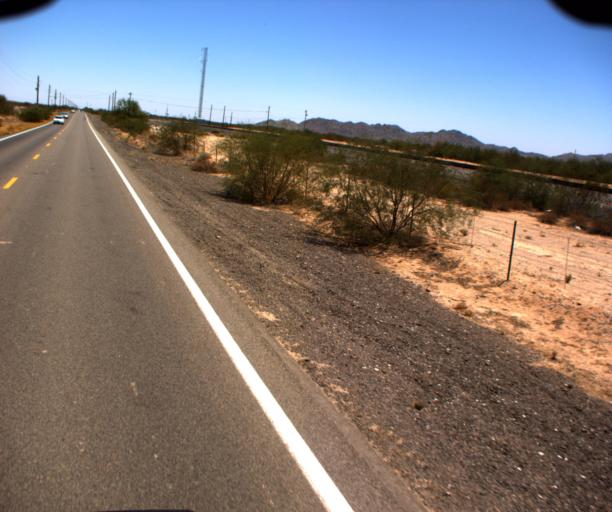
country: US
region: Arizona
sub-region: Pinal County
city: Maricopa
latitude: 33.0634
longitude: -112.2403
